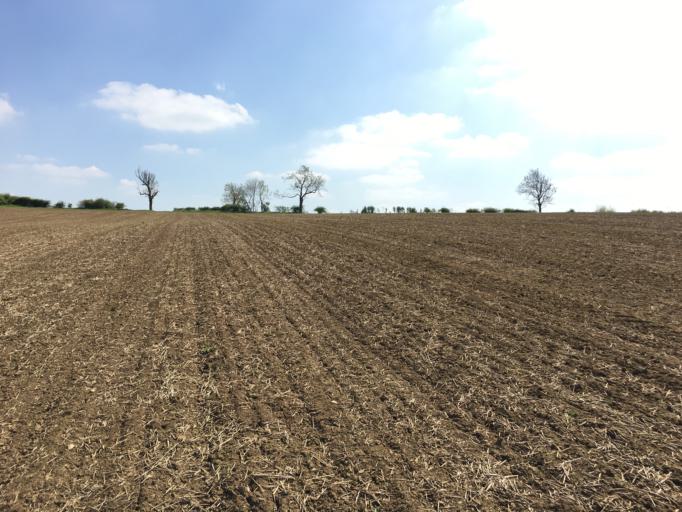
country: GB
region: England
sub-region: Leicestershire
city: Houghton on the Hill
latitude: 52.6107
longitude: -0.9868
